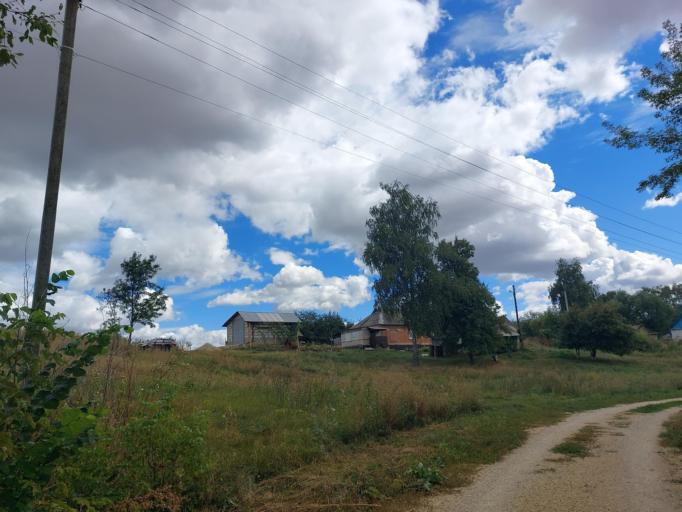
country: RU
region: Lipetsk
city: Terbuny
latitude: 52.2602
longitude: 38.2080
